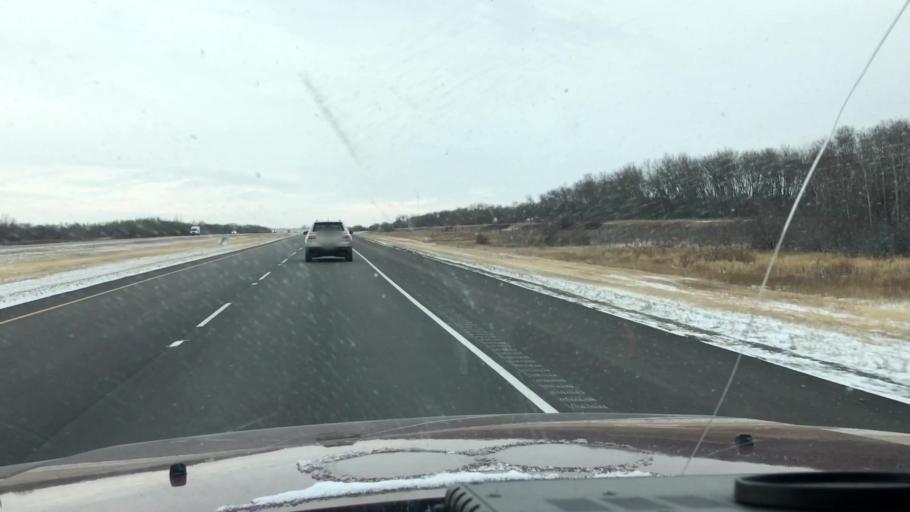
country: CA
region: Saskatchewan
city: Saskatoon
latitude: 51.8790
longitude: -106.5116
